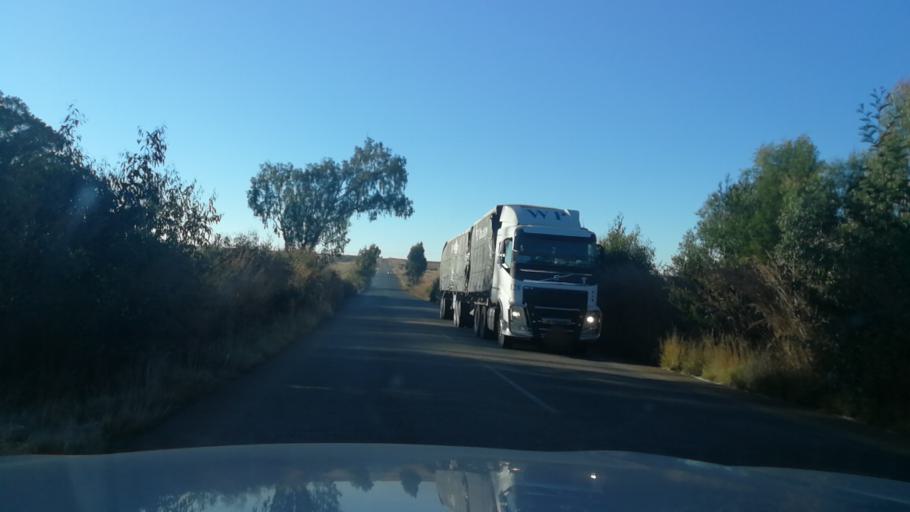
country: ZA
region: North-West
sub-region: Bojanala Platinum District Municipality
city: Rustenburg
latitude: -25.9602
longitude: 27.2035
